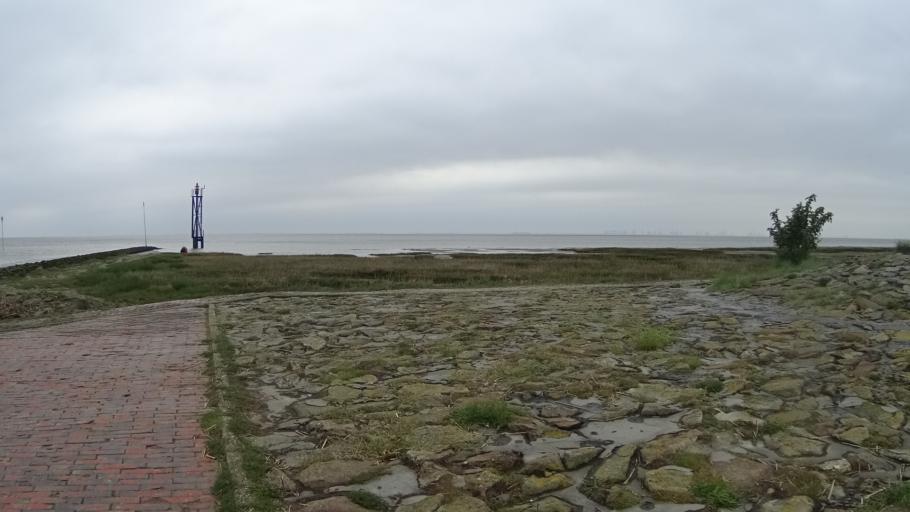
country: DE
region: Lower Saxony
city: Butjadingen
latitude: 53.5986
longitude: 8.3573
